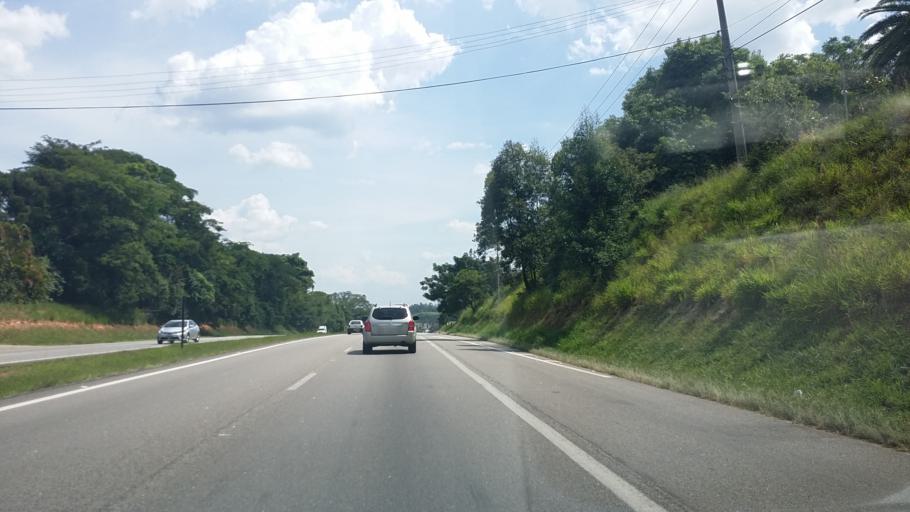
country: BR
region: Sao Paulo
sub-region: Itupeva
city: Itupeva
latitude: -23.2128
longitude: -47.0169
